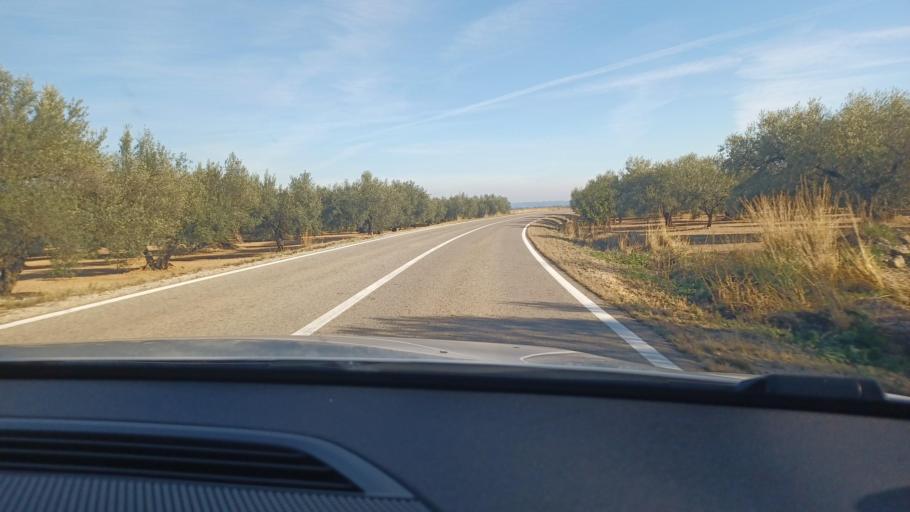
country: ES
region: Catalonia
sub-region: Provincia de Tarragona
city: Santa Barbara
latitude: 40.7222
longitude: 0.4379
